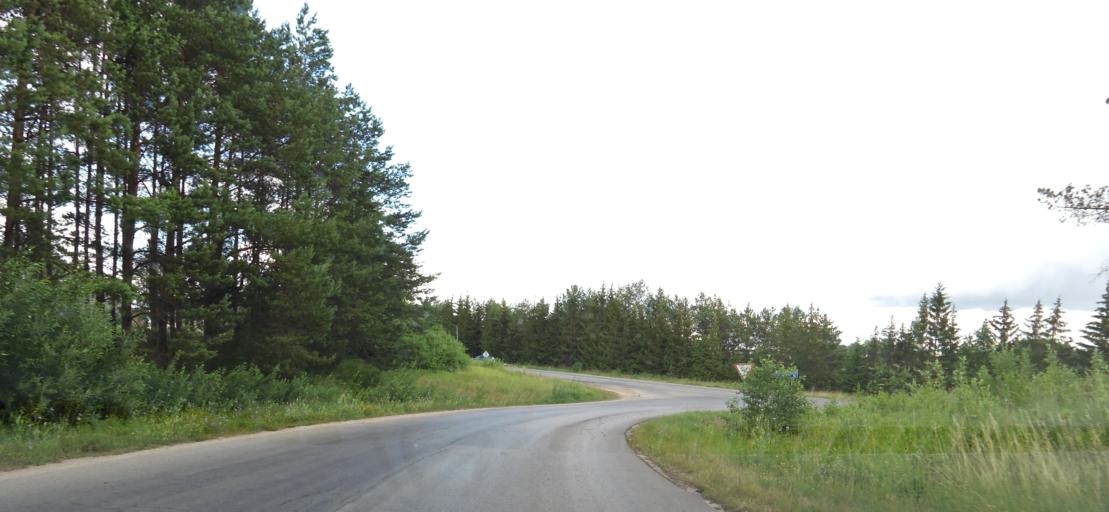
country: LT
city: Kupiskis
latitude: 55.8482
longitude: 24.9638
